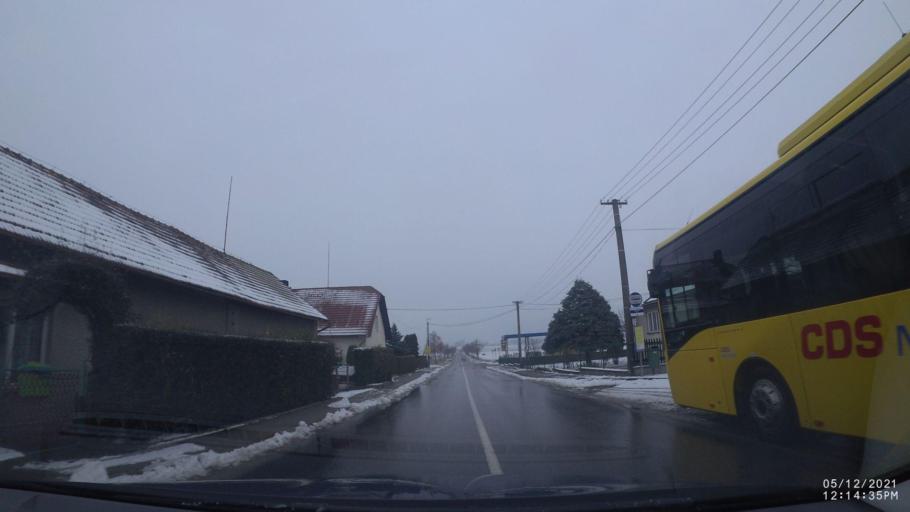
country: CZ
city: Ceske Mezirici
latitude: 50.3065
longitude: 16.0331
